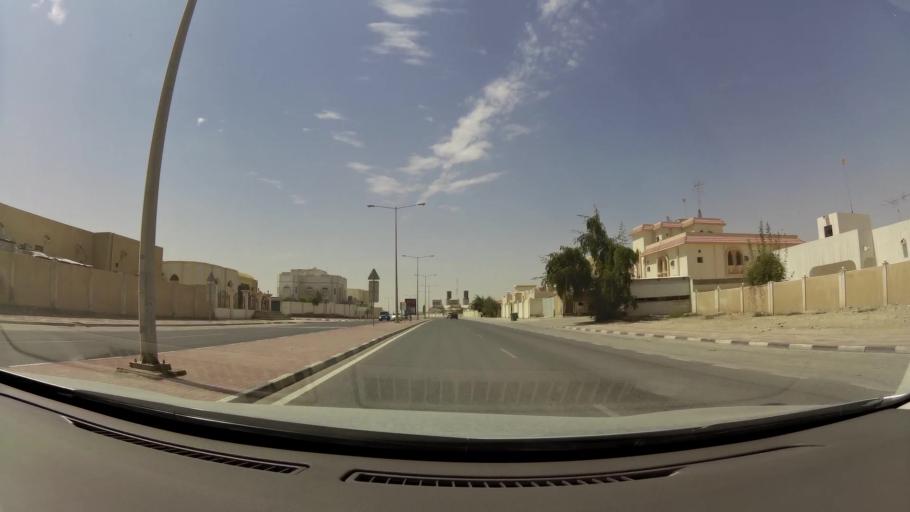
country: QA
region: Baladiyat ar Rayyan
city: Ar Rayyan
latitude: 25.2997
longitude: 51.4108
